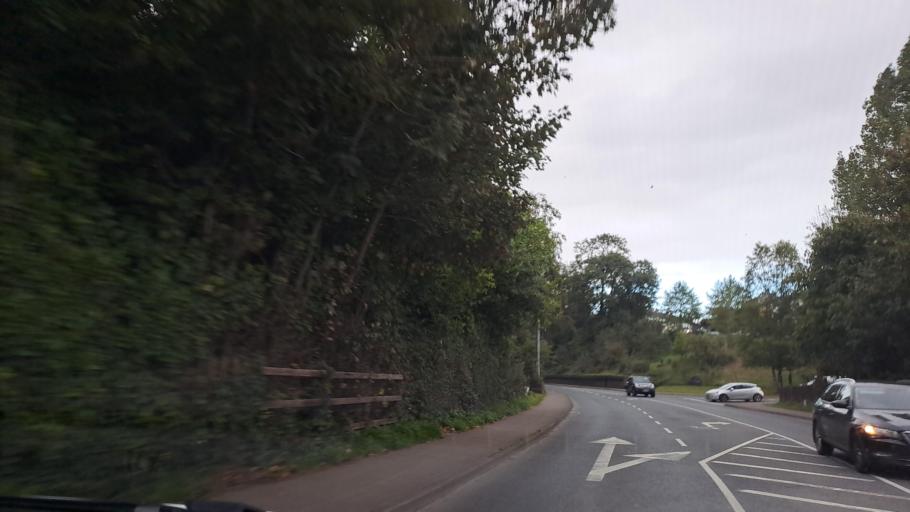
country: IE
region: Ulster
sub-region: County Monaghan
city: Monaghan
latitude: 54.2393
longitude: -6.9685
